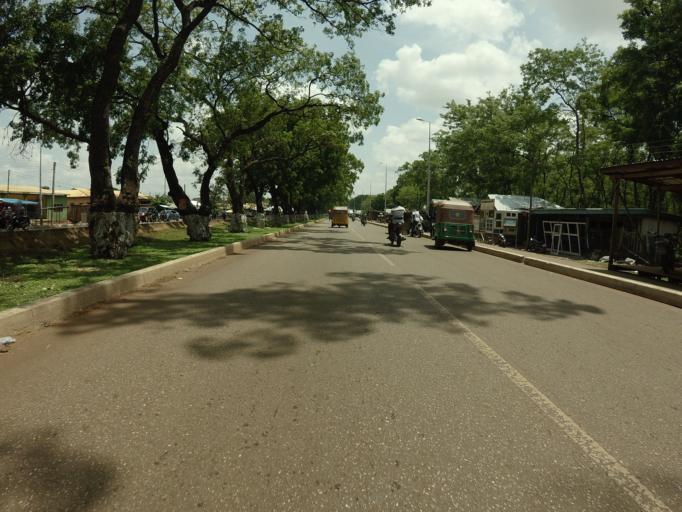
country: GH
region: Northern
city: Tamale
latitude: 9.4044
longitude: -0.8532
